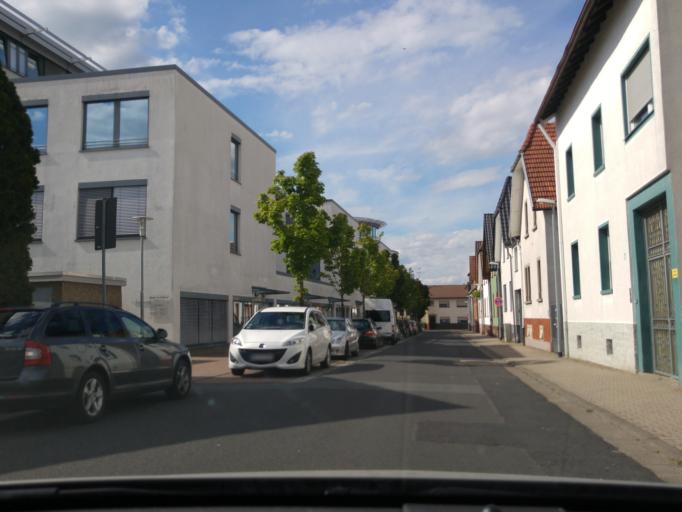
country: DE
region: Hesse
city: Dreieich
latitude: 50.0178
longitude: 8.6969
